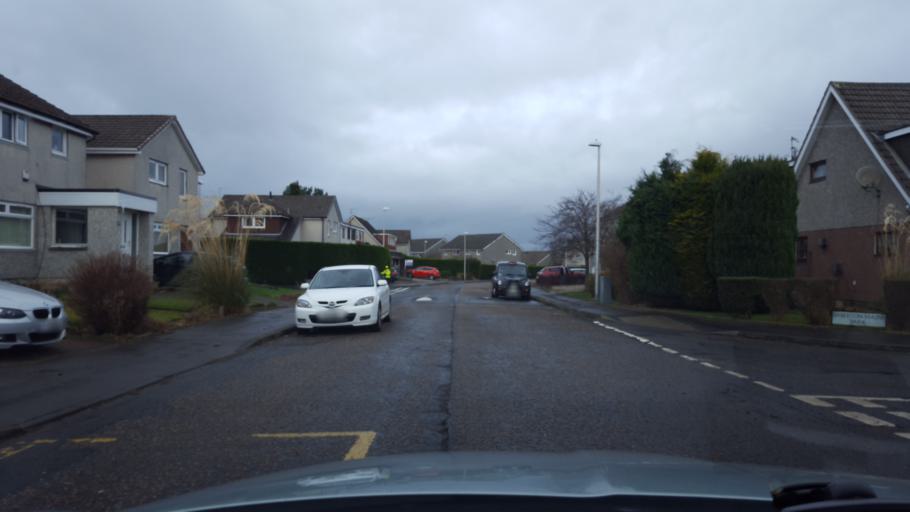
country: GB
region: Scotland
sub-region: Edinburgh
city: Currie
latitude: 55.9093
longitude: -3.2891
